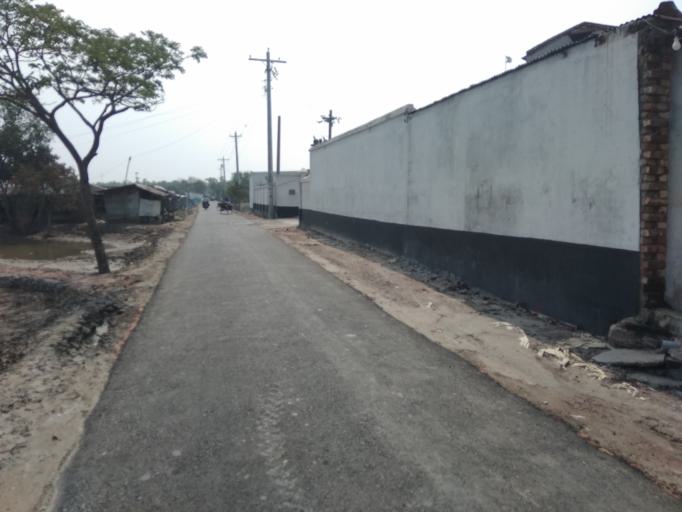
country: IN
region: West Bengal
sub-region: North 24 Parganas
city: Gosaba
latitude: 22.2623
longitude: 89.2229
